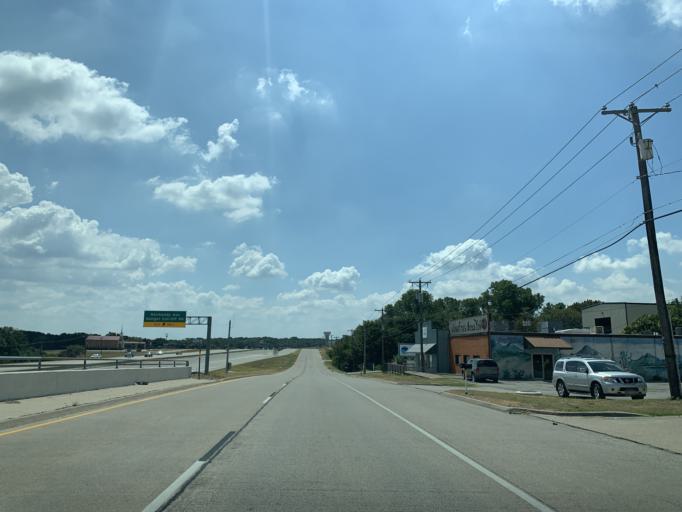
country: US
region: Texas
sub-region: Tarrant County
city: Azle
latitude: 32.8748
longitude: -97.5303
